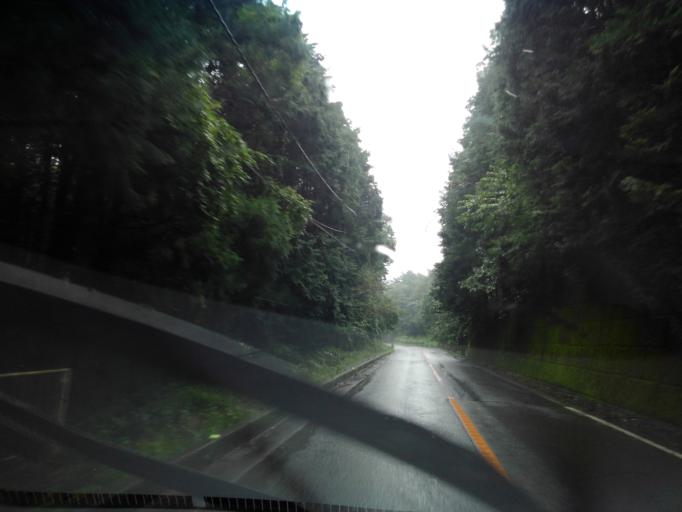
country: JP
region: Saitama
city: Hanno
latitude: 35.8248
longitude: 139.3397
